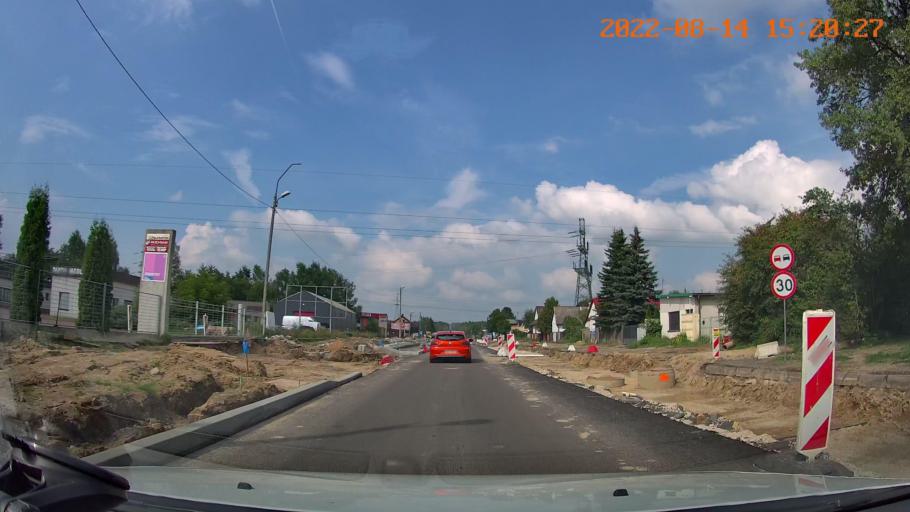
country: PL
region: Swietokrzyskie
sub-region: Powiat kielecki
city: Kielce
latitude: 50.9037
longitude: 20.6353
